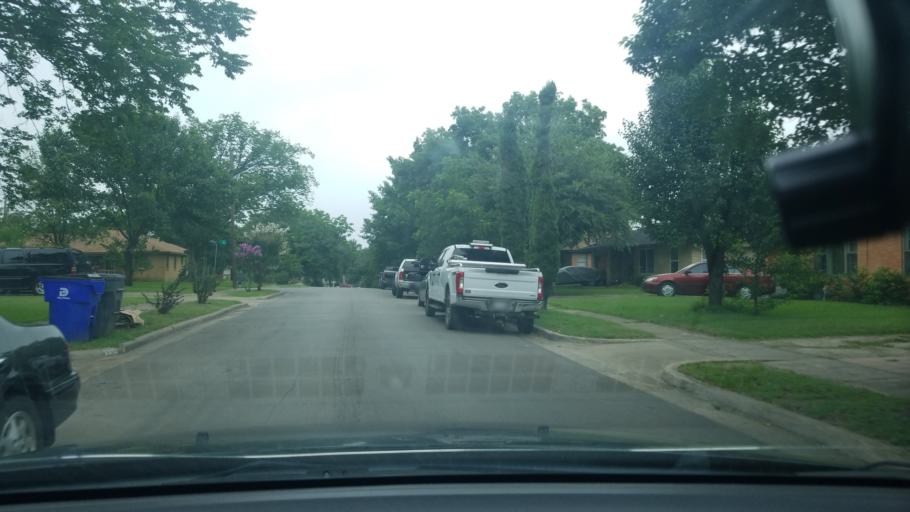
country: US
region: Texas
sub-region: Dallas County
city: Balch Springs
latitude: 32.7540
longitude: -96.6936
